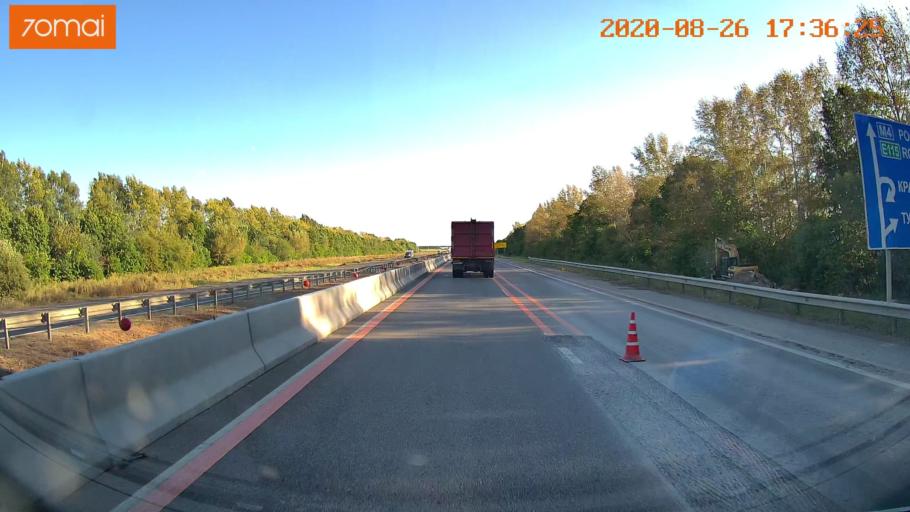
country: RU
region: Tula
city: Kazachka
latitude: 53.3720
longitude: 38.1834
